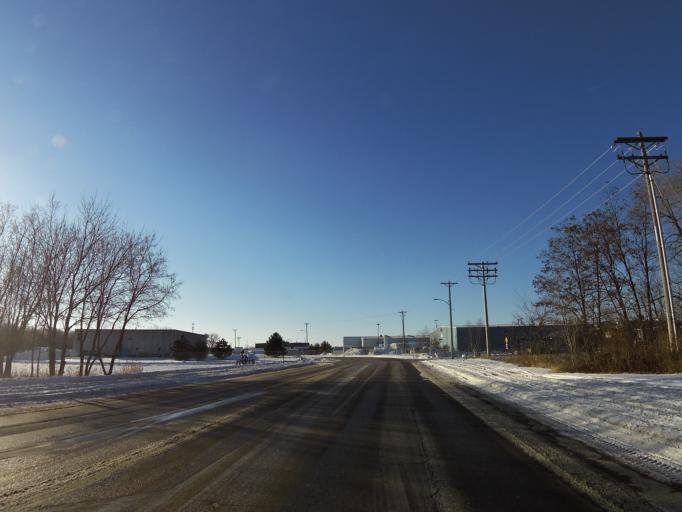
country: US
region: Minnesota
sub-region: Le Sueur County
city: New Prague
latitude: 44.5510
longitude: -93.5784
